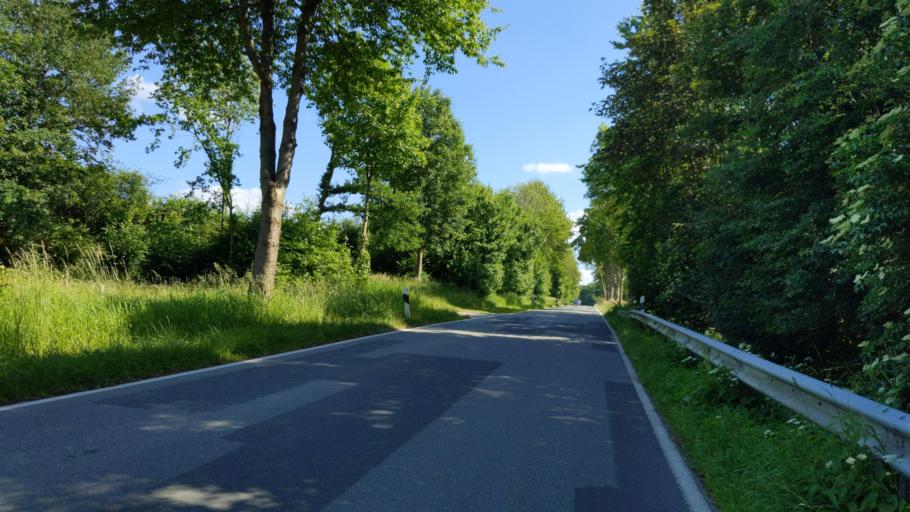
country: DE
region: Schleswig-Holstein
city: Goldenitz
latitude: 53.7113
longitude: 10.6493
